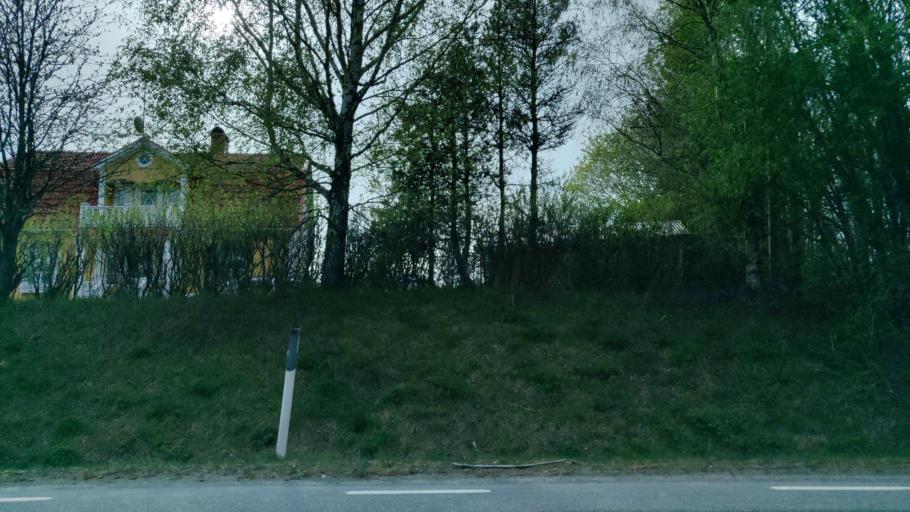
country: SE
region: Vaermland
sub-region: Munkfors Kommun
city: Munkfors
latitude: 59.7990
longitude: 13.5038
